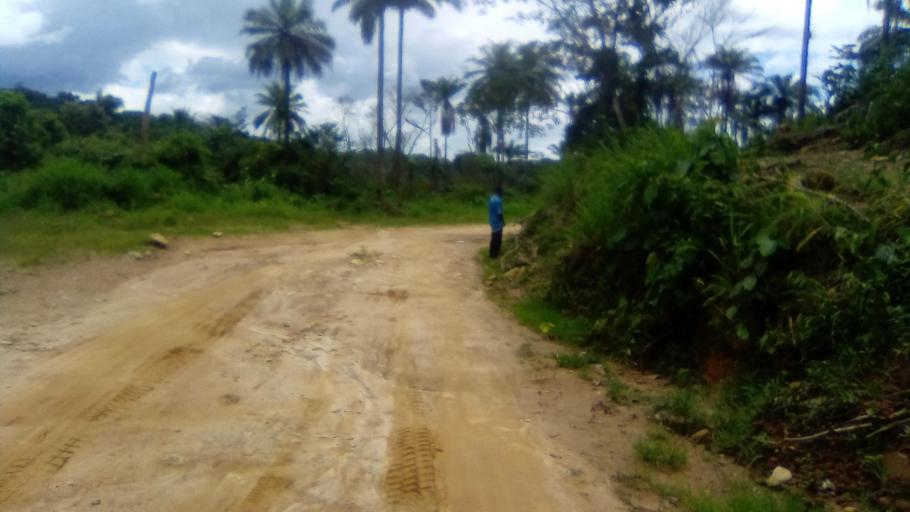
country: SL
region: Eastern Province
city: Simbakoro
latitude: 8.5279
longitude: -10.9087
